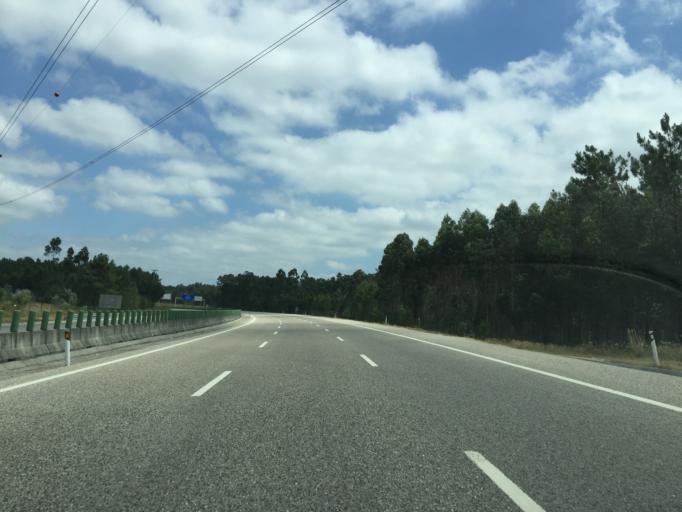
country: PT
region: Leiria
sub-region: Leiria
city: Monte Redondo
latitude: 39.9359
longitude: -8.7721
